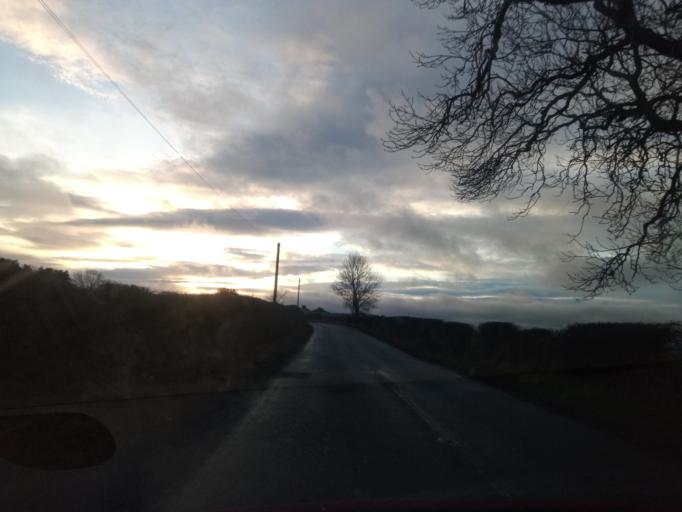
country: GB
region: England
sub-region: Northumberland
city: Meldon
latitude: 55.1380
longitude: -1.7557
